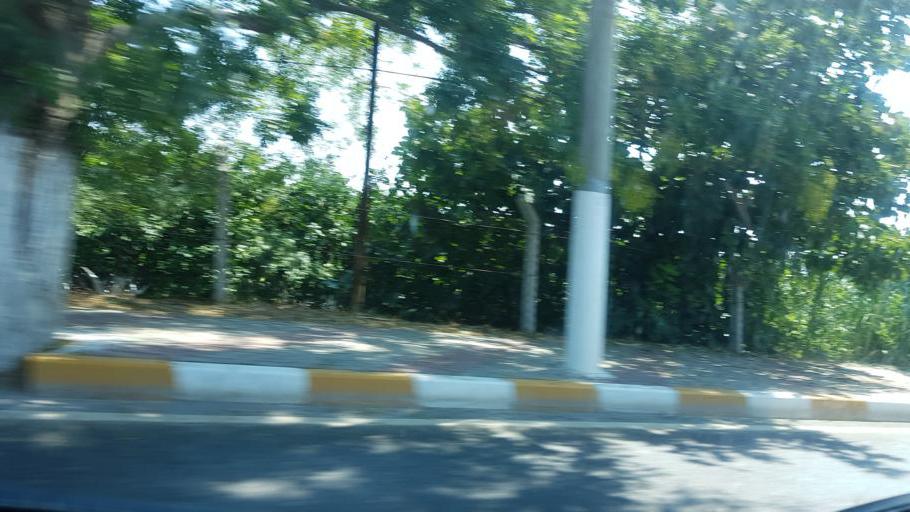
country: TR
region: Izmir
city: Urla
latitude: 38.3485
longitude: 26.7717
